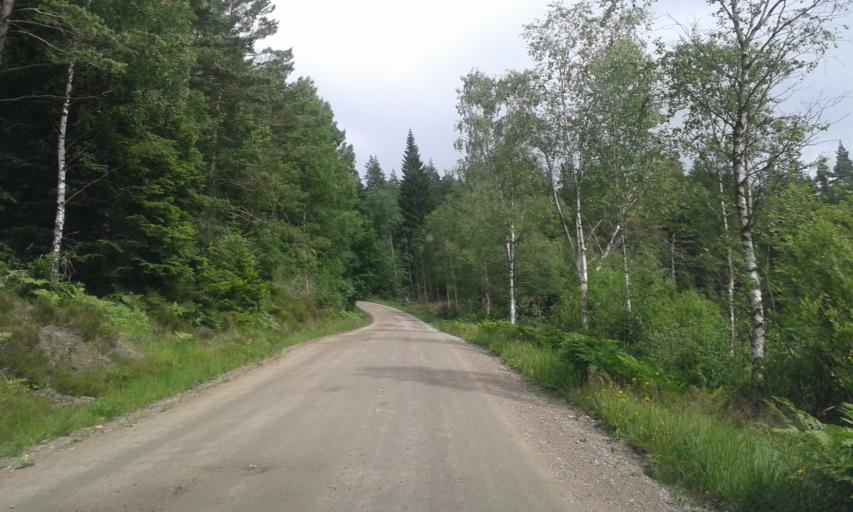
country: SE
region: Vaestra Goetaland
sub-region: Kungalvs Kommun
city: Diserod
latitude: 57.9872
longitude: 12.0195
